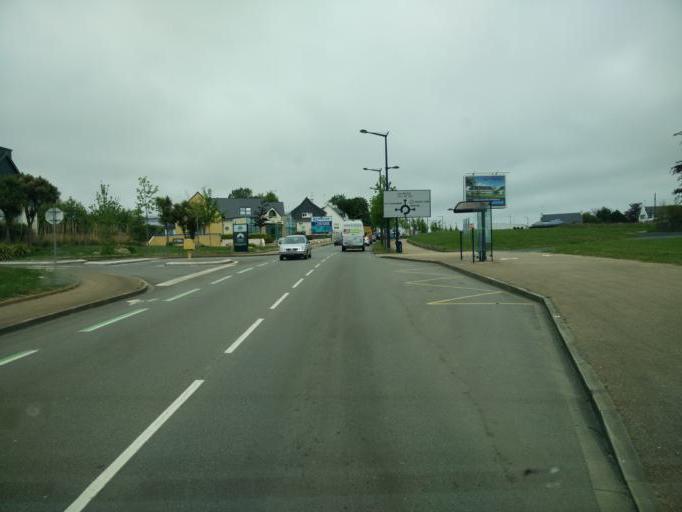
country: FR
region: Brittany
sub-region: Departement du Finistere
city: Concarneau
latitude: 47.8860
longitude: -3.9197
